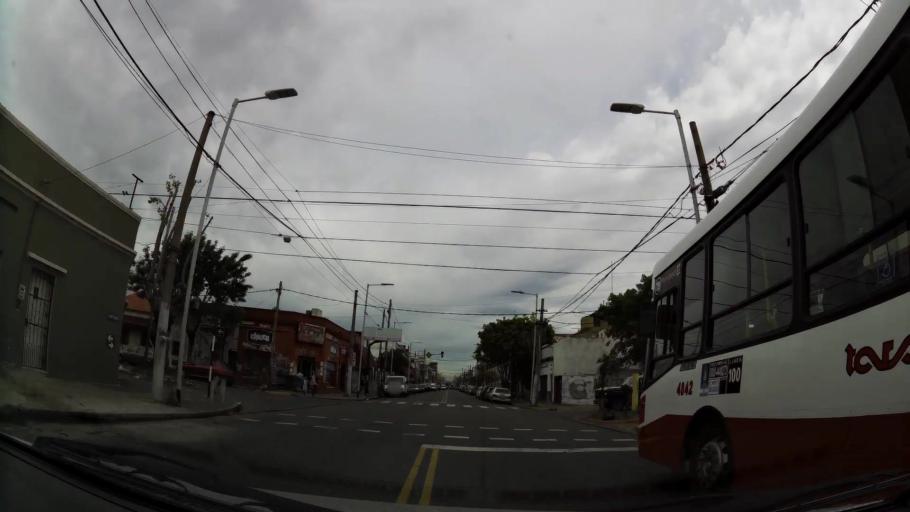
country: AR
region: Buenos Aires
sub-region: Partido de Avellaneda
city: Avellaneda
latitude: -34.6834
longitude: -58.3722
